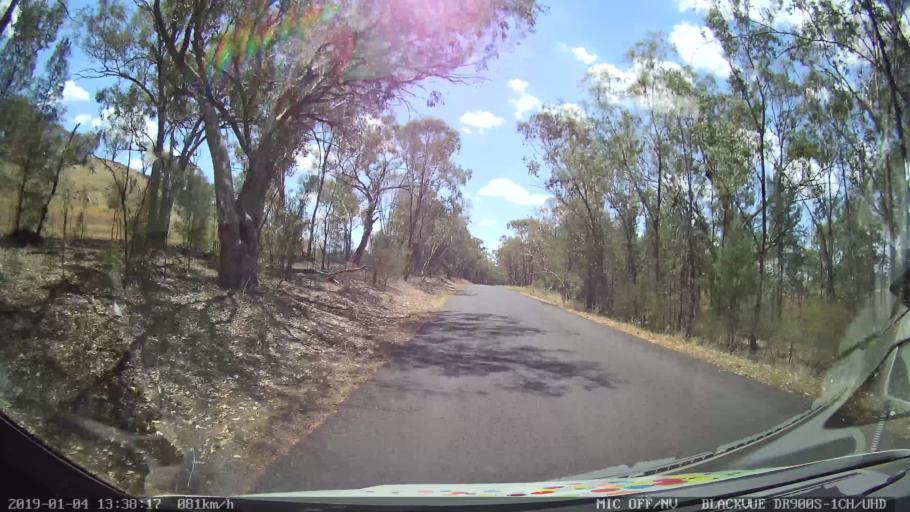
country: AU
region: New South Wales
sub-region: Dubbo Municipality
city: Dubbo
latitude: -32.5398
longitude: 148.5470
